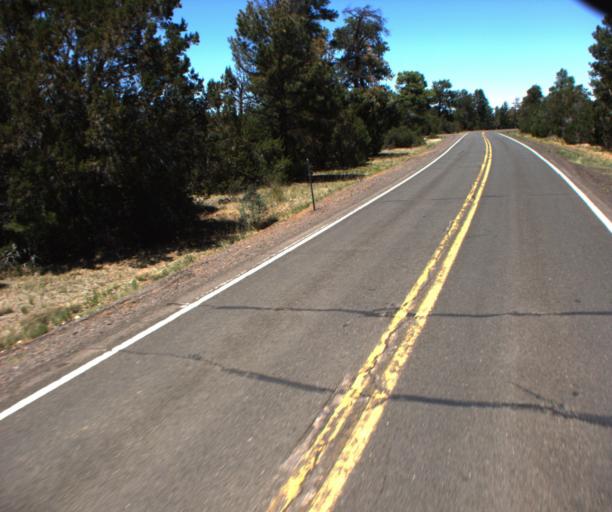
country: US
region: Arizona
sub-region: Gila County
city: Star Valley
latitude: 34.6723
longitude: -111.1092
